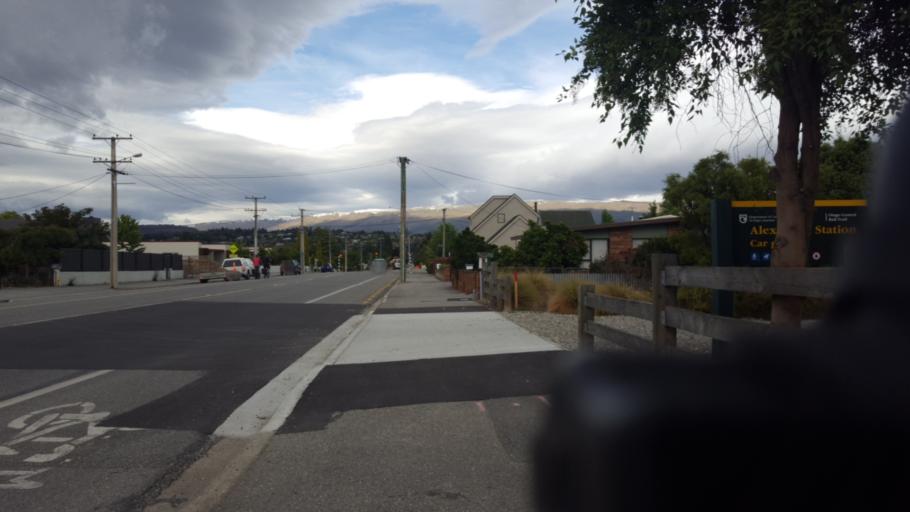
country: NZ
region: Otago
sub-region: Queenstown-Lakes District
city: Wanaka
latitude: -45.2491
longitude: 169.3984
